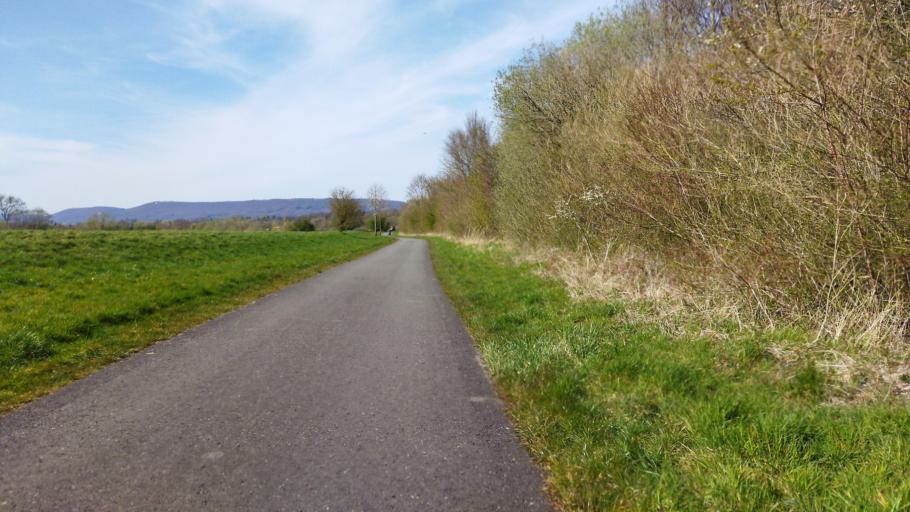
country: DE
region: Lower Saxony
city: Hessisch Oldendorf
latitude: 52.1583
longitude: 9.2696
